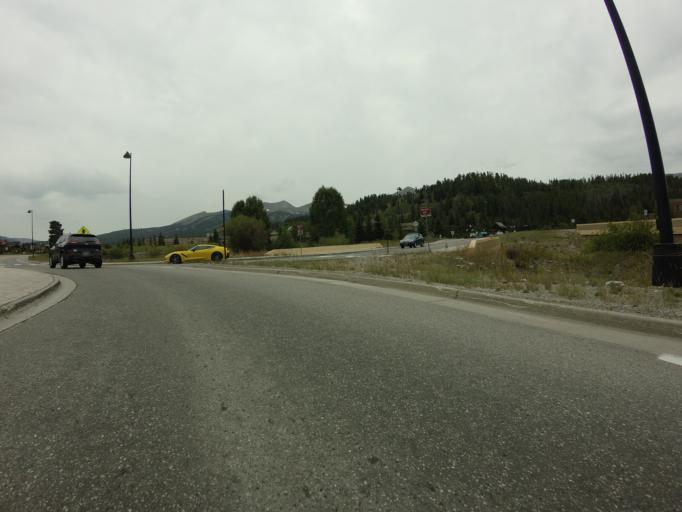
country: US
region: Colorado
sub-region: Summit County
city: Breckenridge
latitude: 39.4906
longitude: -106.0458
